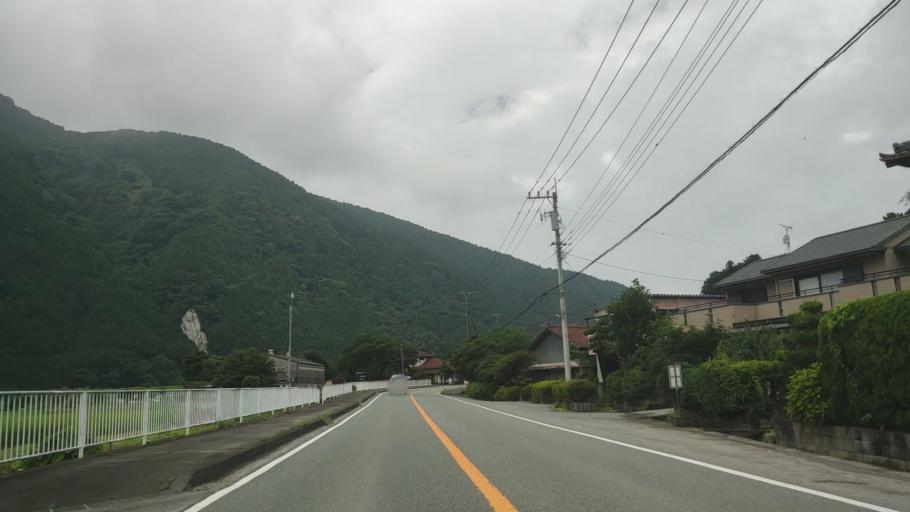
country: JP
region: Shizuoka
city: Fujinomiya
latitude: 35.2111
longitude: 138.5466
